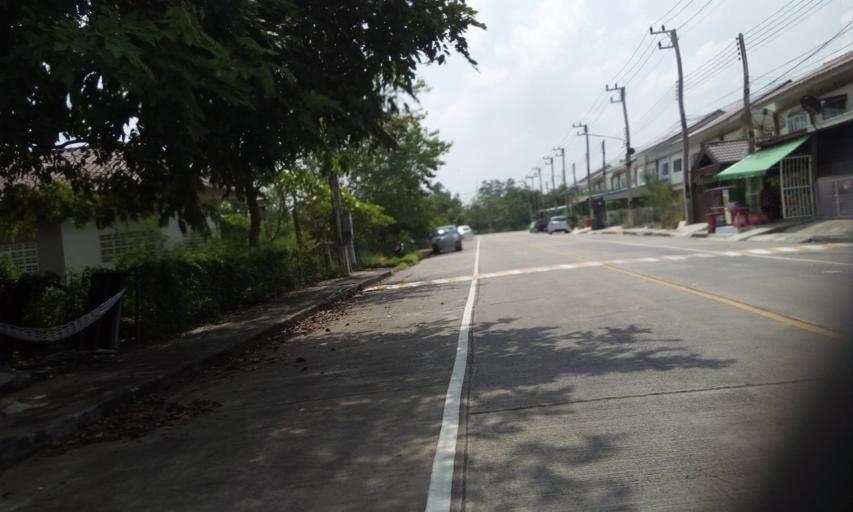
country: TH
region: Pathum Thani
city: Ban Rangsit
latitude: 14.0549
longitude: 100.8224
